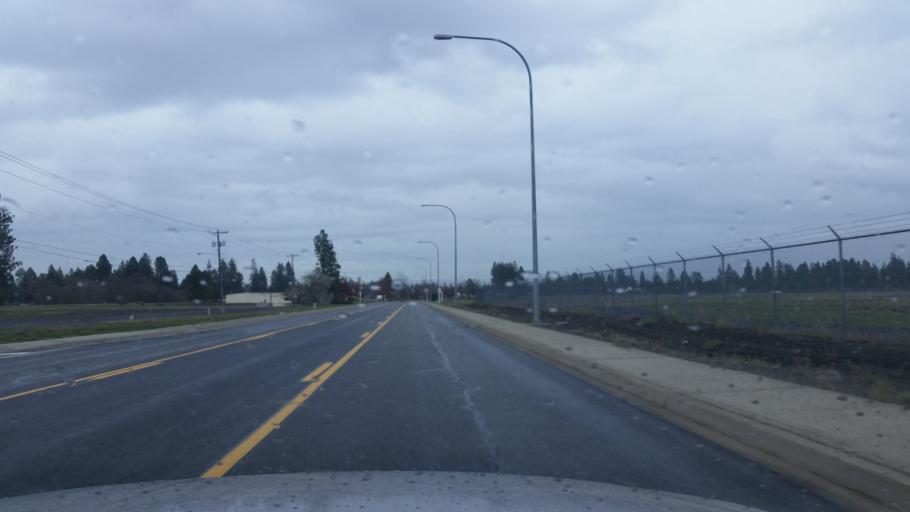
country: US
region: Washington
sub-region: Spokane County
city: Airway Heights
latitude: 47.6190
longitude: -117.5162
